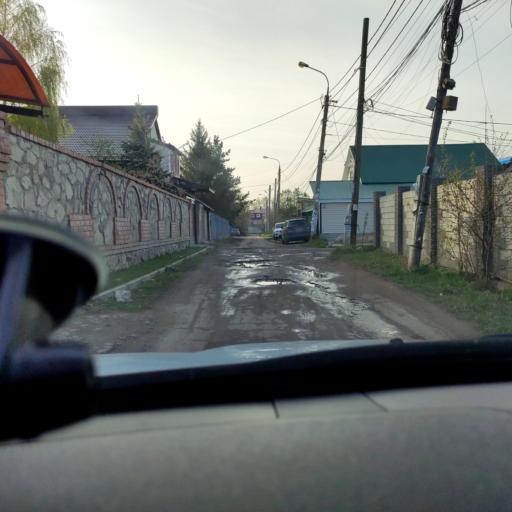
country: RU
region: Samara
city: Volzhskiy
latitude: 53.3548
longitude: 50.2135
